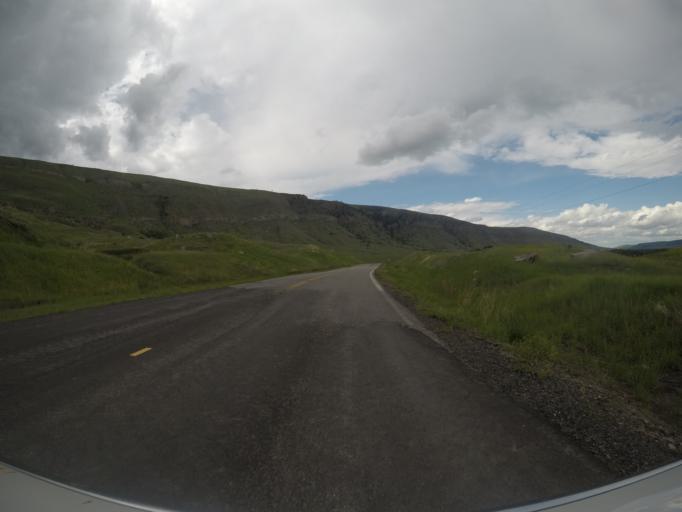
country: US
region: Montana
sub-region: Sweet Grass County
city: Big Timber
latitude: 45.5679
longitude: -110.2018
